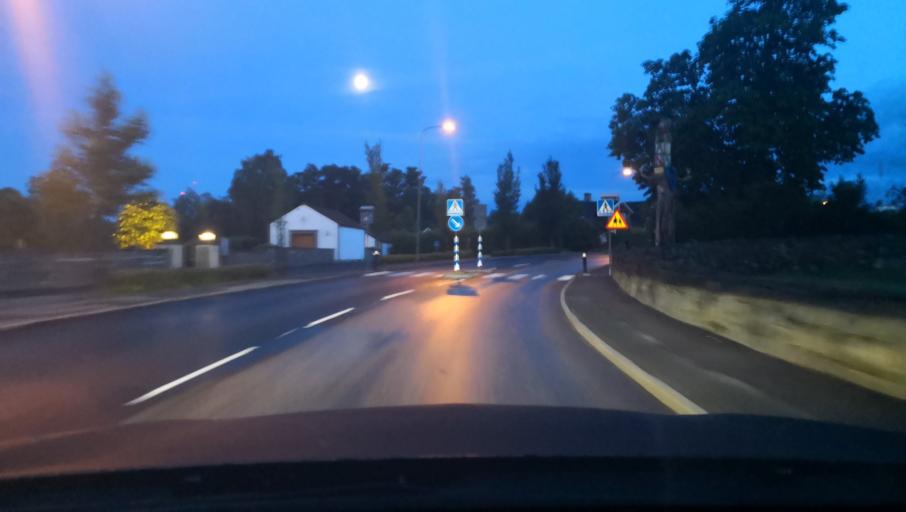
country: SE
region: Skane
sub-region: Osby Kommun
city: Osby
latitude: 56.3811
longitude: 14.0003
